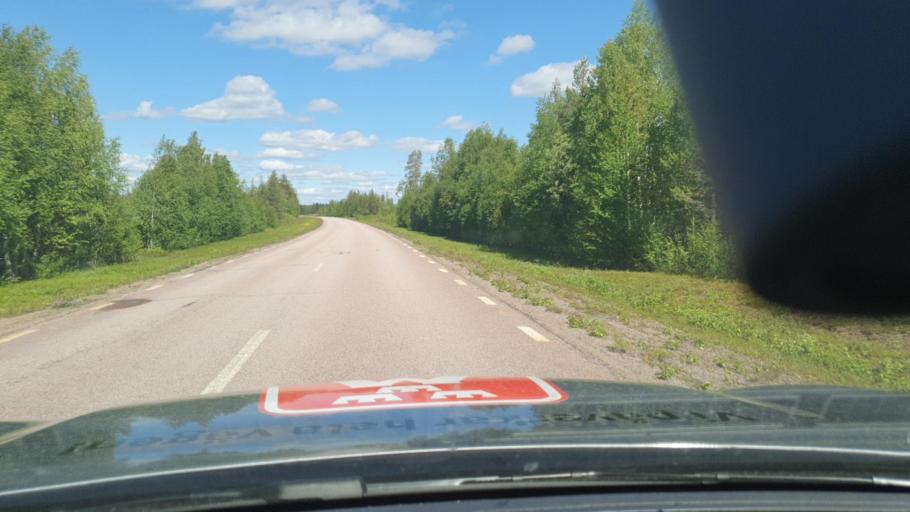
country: SE
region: Norrbotten
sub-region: Pajala Kommun
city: Pajala
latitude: 67.2259
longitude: 22.7862
